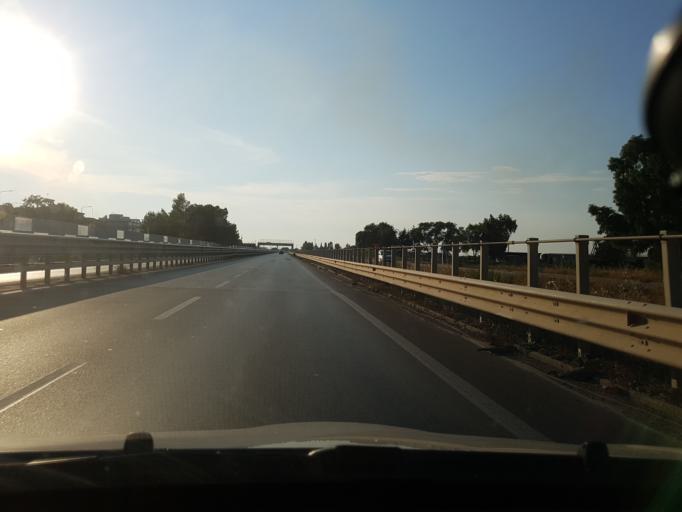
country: IT
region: Apulia
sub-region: Provincia di Foggia
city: Carapelle
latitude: 41.3652
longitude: 15.6996
